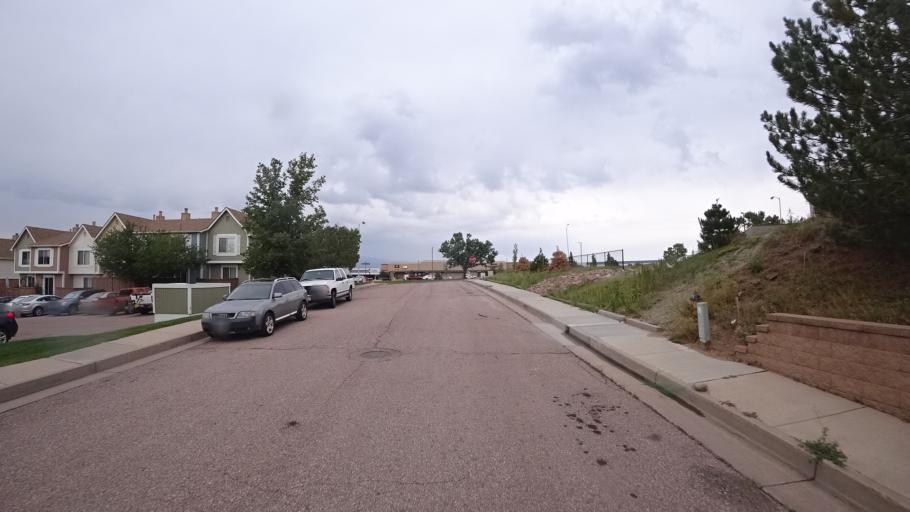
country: US
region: Colorado
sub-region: El Paso County
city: Colorado Springs
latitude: 38.9250
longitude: -104.7952
